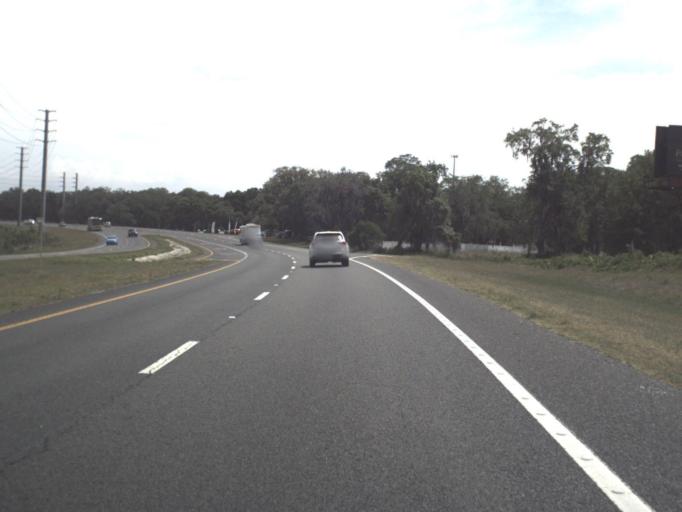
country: US
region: Florida
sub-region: Sumter County
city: Wildwood
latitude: 28.8247
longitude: -81.9892
